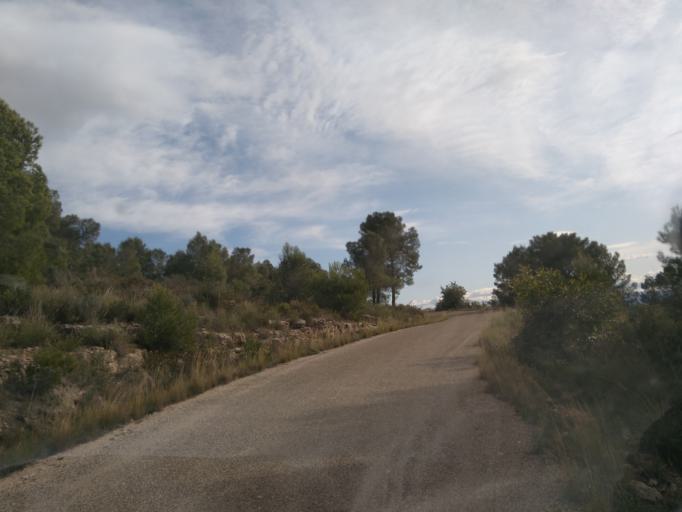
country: ES
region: Valencia
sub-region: Provincia de Valencia
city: Sumacarcer
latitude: 39.1472
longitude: -0.6414
